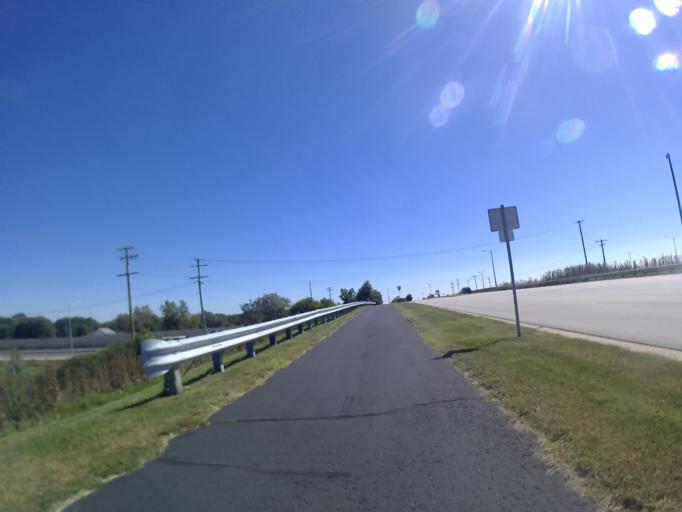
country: US
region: Illinois
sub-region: Cook County
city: Lemont
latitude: 41.7089
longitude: -88.0250
